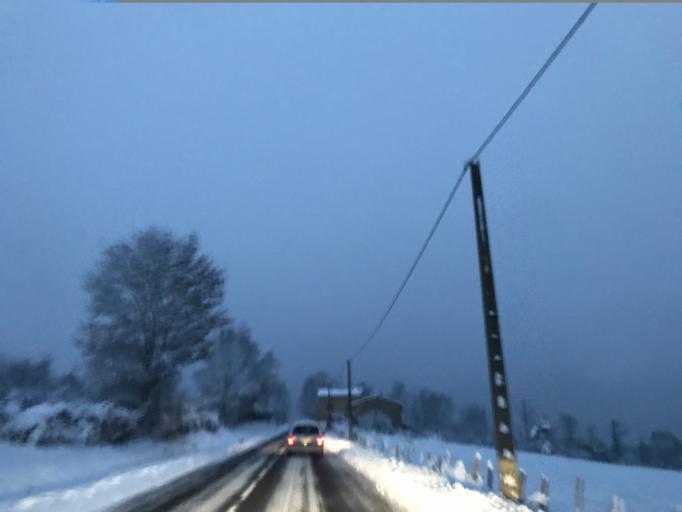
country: FR
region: Auvergne
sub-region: Departement du Puy-de-Dome
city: Courpiere
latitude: 45.7194
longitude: 3.5880
